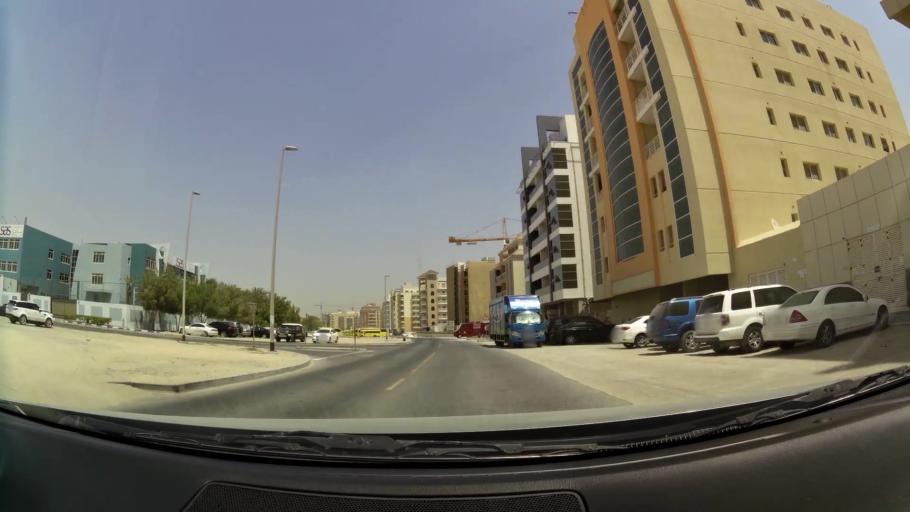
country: AE
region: Ash Shariqah
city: Sharjah
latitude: 25.1901
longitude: 55.4030
